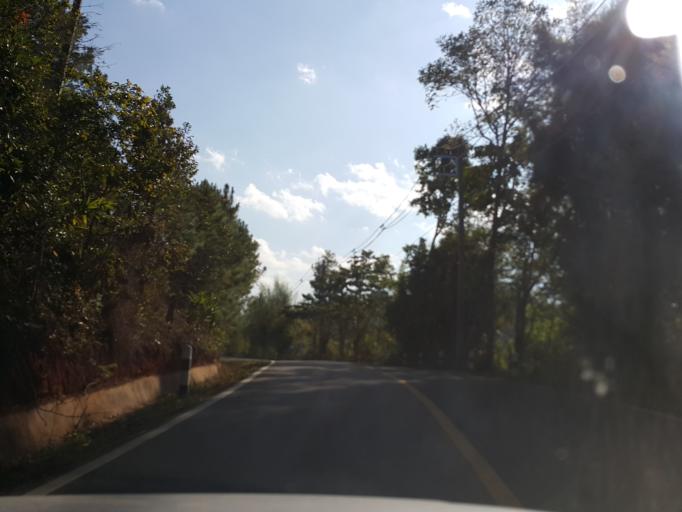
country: TH
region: Chiang Mai
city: Mae Wang
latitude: 18.6763
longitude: 98.5533
